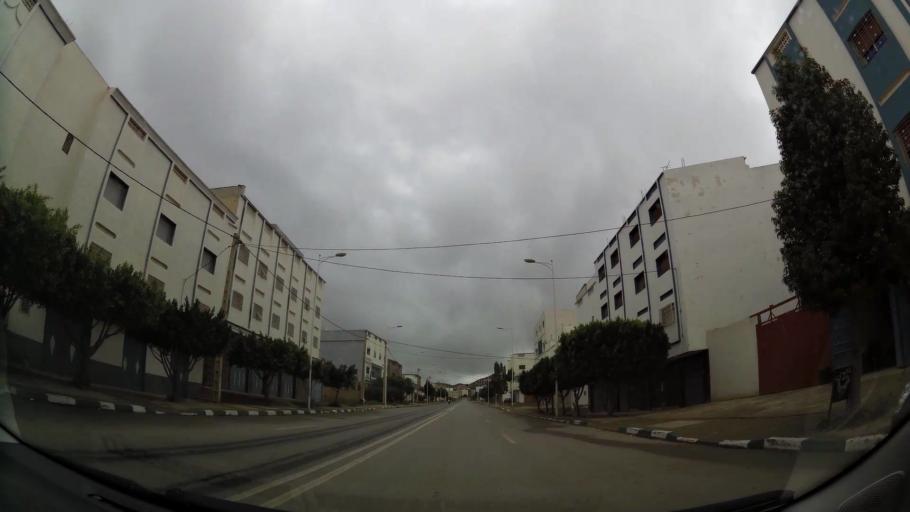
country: MA
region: Oriental
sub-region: Nador
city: Midar
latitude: 35.0518
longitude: -3.4610
